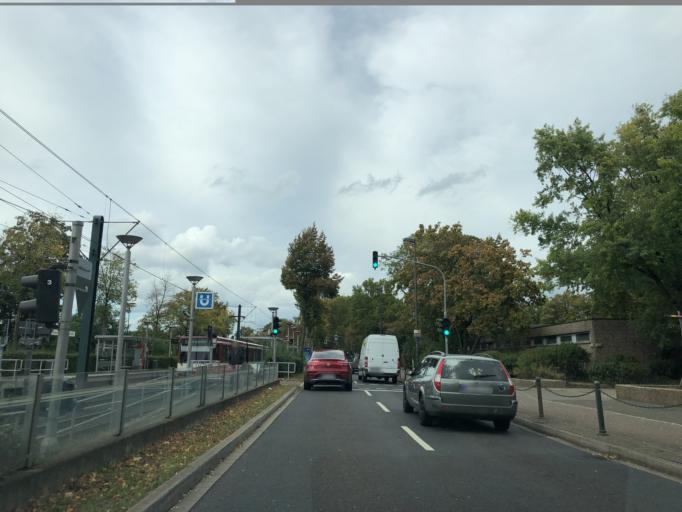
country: DE
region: North Rhine-Westphalia
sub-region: Regierungsbezirk Dusseldorf
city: Dusseldorf
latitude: 51.2029
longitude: 6.8109
